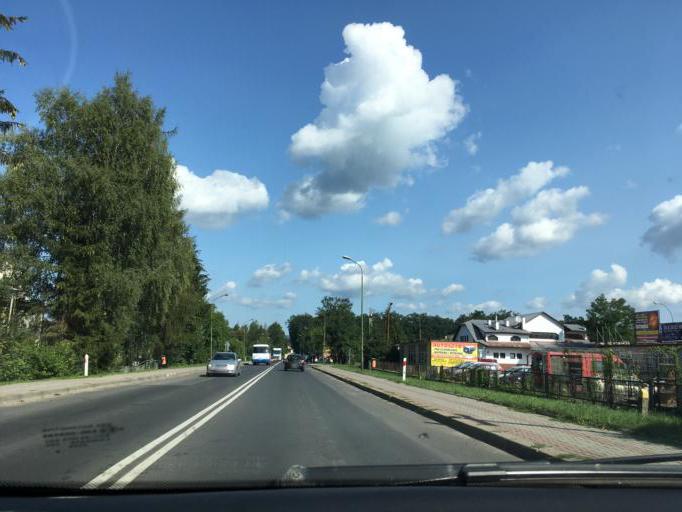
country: PL
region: Subcarpathian Voivodeship
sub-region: Powiat leski
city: Lesko
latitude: 49.4749
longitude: 22.3251
